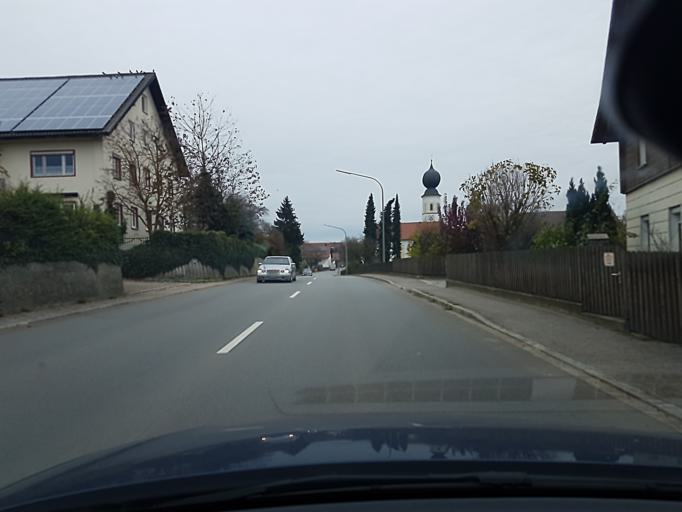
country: DE
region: Bavaria
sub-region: Lower Bavaria
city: Ergoldsbach
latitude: 48.7089
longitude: 12.1937
